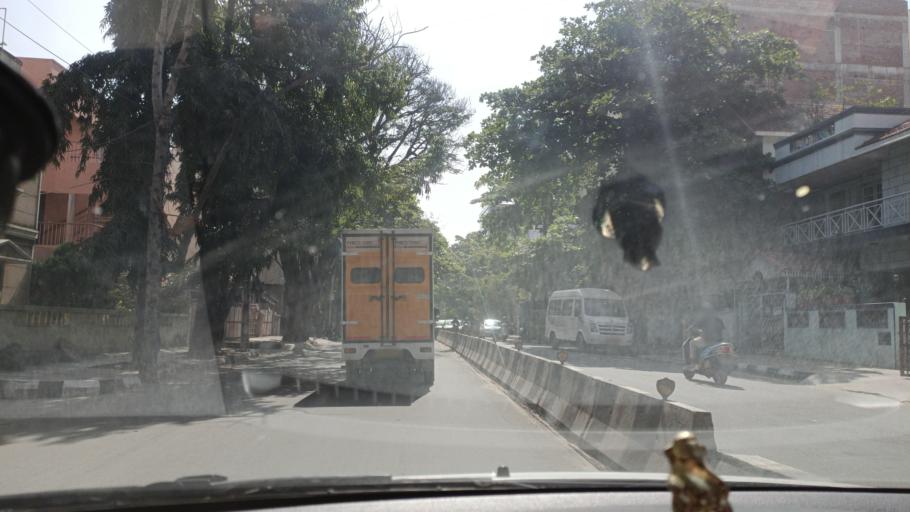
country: IN
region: Karnataka
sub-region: Bangalore Urban
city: Bangalore
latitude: 12.9138
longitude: 77.6151
